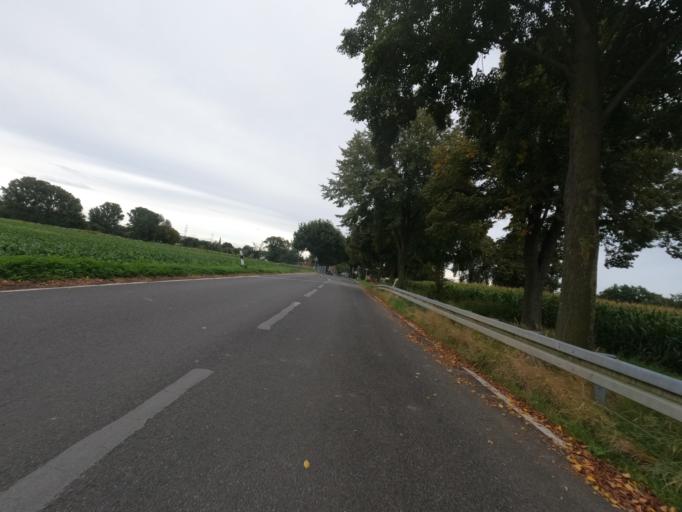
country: DE
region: North Rhine-Westphalia
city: Baesweiler
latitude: 50.9395
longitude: 6.2014
